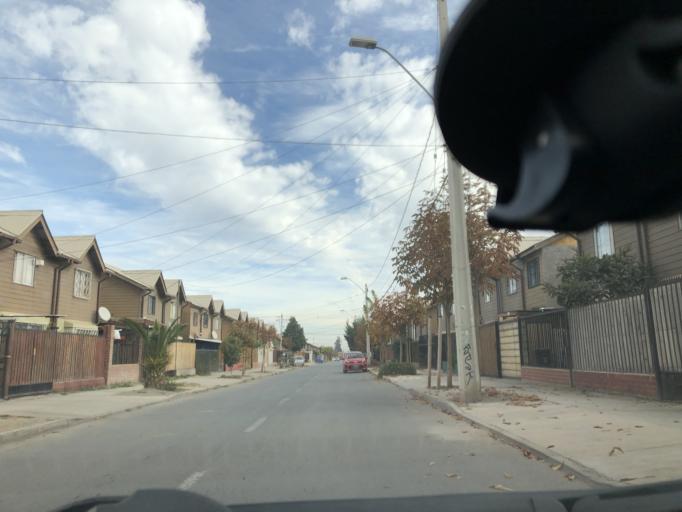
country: CL
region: Santiago Metropolitan
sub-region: Provincia de Cordillera
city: Puente Alto
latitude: -33.6120
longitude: -70.5250
